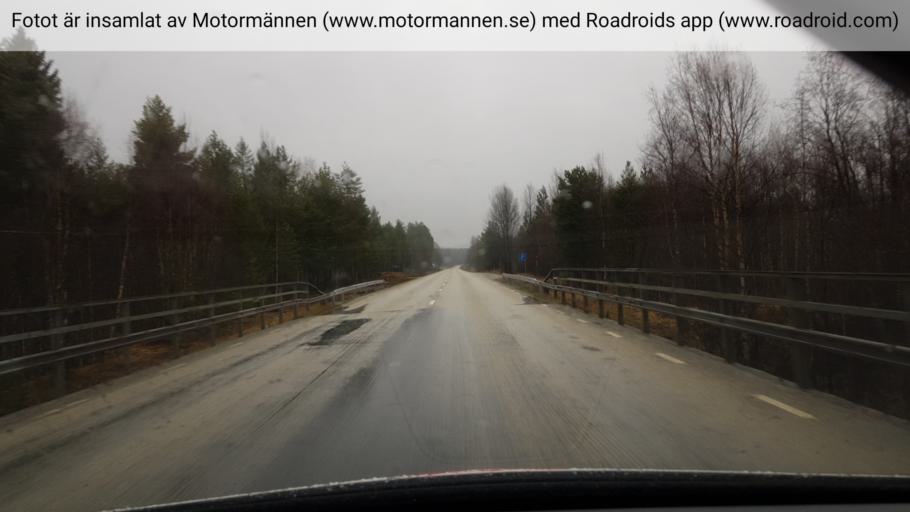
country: SE
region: Jaemtland
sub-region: Harjedalens Kommun
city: Sveg
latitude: 62.4314
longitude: 13.8343
